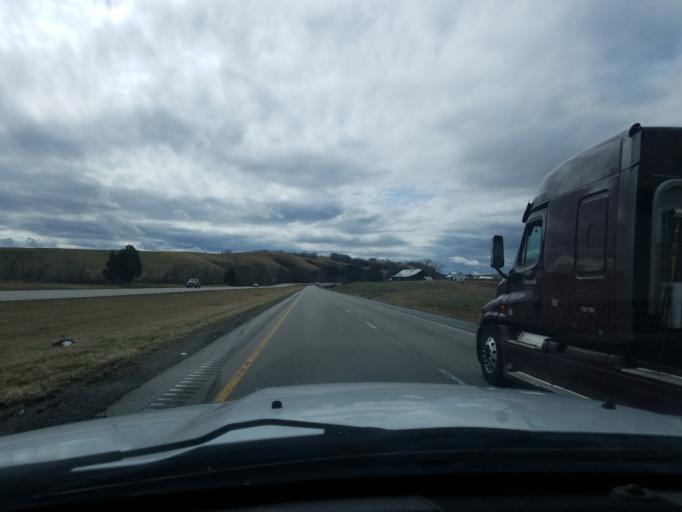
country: US
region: Kentucky
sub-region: Bath County
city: Owingsville
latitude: 38.1164
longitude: -83.8011
